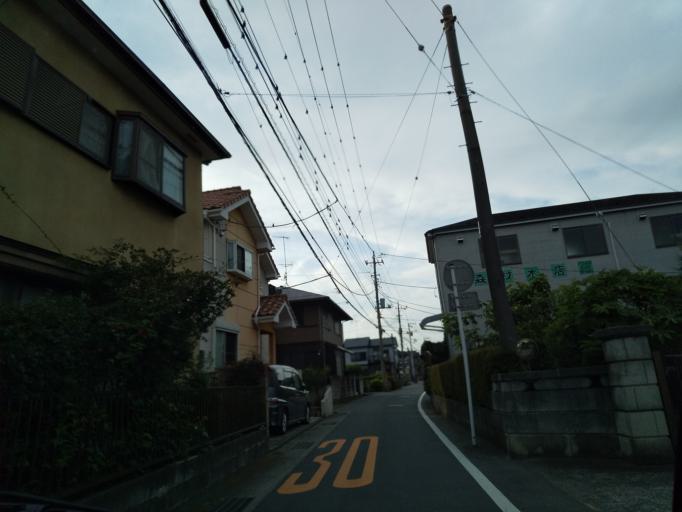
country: JP
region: Kanagawa
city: Zama
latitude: 35.5053
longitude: 139.3623
